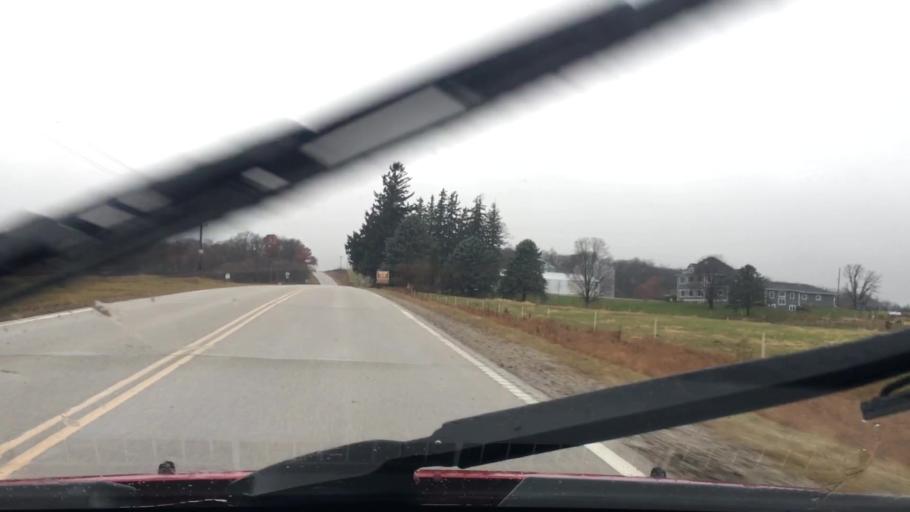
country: US
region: Minnesota
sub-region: Fillmore County
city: Preston
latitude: 43.7331
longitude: -92.0018
